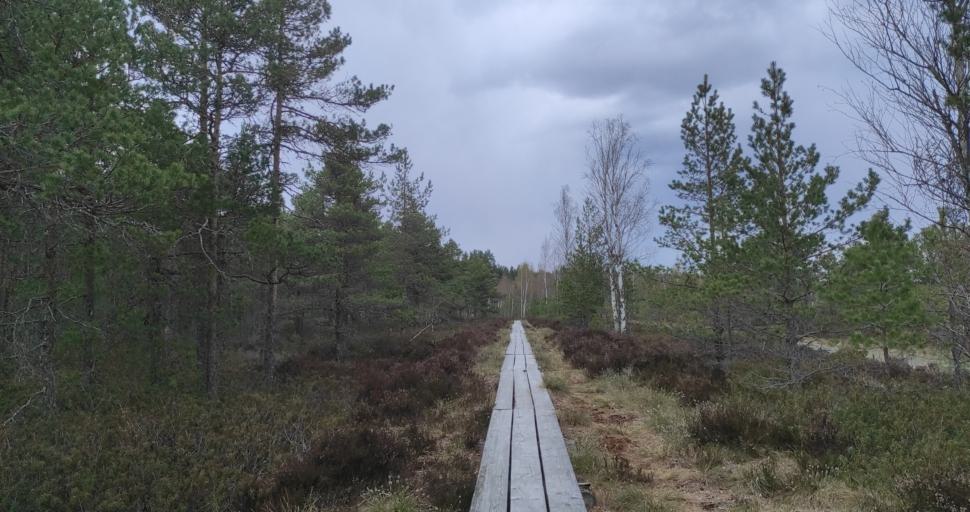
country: LV
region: Dundaga
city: Dundaga
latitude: 57.3518
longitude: 22.1501
